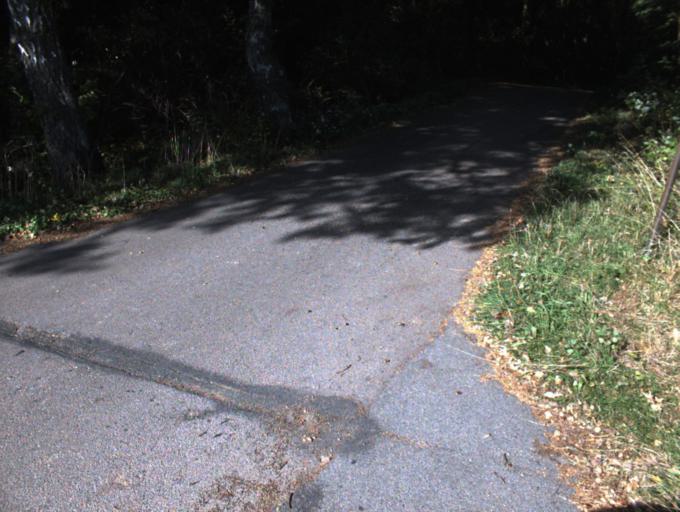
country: SE
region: Skane
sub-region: Helsingborg
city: Helsingborg
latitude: 56.0718
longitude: 12.6745
